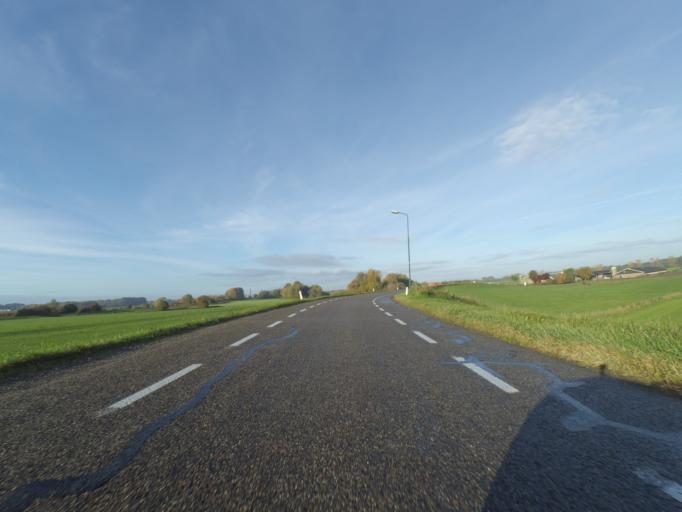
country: NL
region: Utrecht
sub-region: Gemeente Wijk bij Duurstede
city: Wijk bij Duurstede
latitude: 51.9774
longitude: 5.3794
